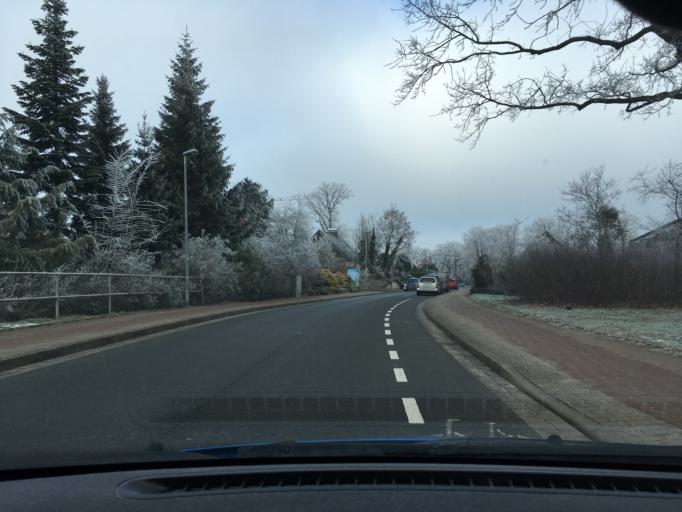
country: DE
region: Lower Saxony
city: Bardowick
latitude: 53.2725
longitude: 10.3891
